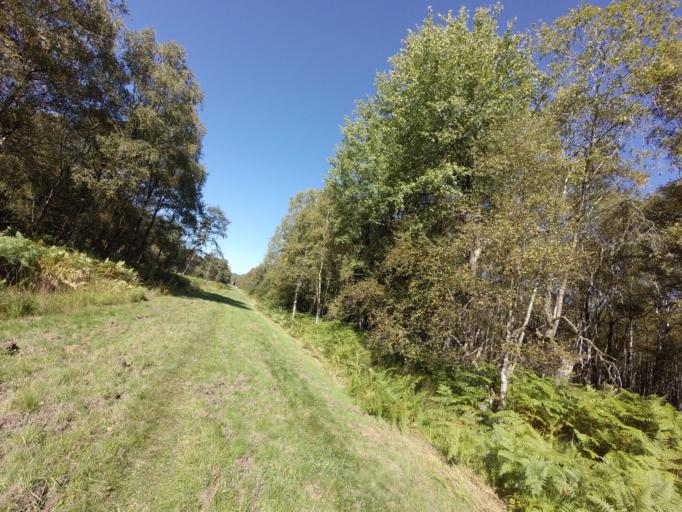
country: DE
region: North Rhine-Westphalia
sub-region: Regierungsbezirk Koln
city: Roetgen
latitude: 50.6033
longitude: 6.1697
